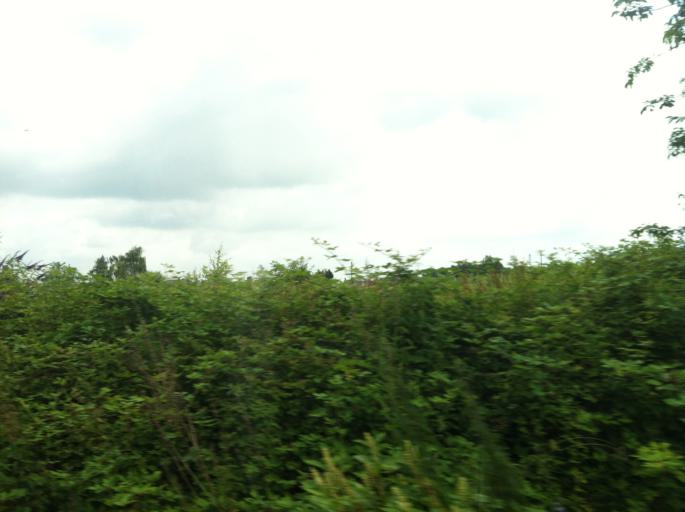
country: DE
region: North Rhine-Westphalia
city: Niederkassel
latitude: 50.8016
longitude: 7.0130
